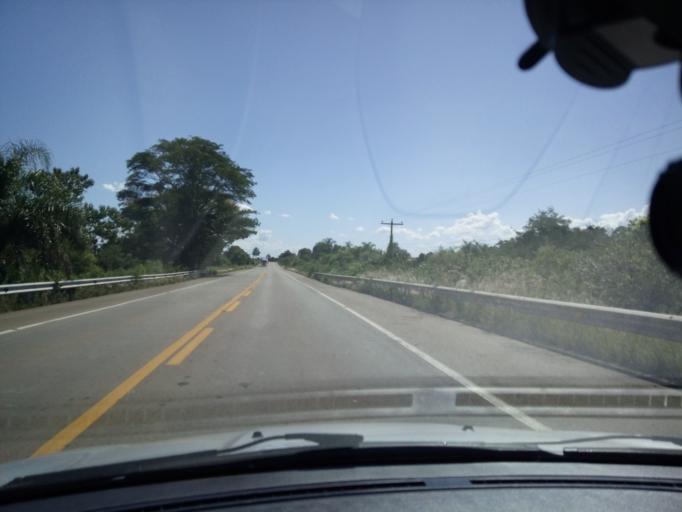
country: BR
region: Rio Grande do Sul
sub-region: Santa Maria
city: Santa Maria
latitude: -29.7324
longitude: -53.5182
